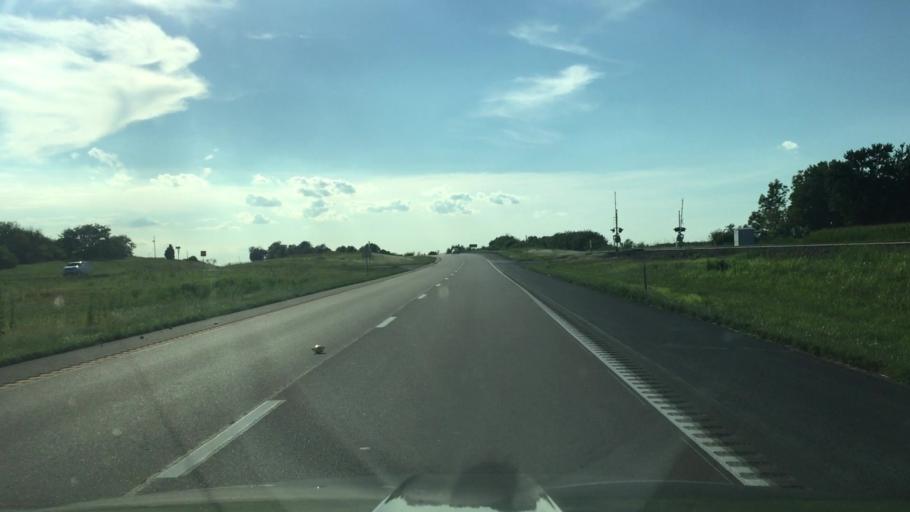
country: US
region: Missouri
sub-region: Pettis County
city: La Monte
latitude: 38.7605
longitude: -93.3734
